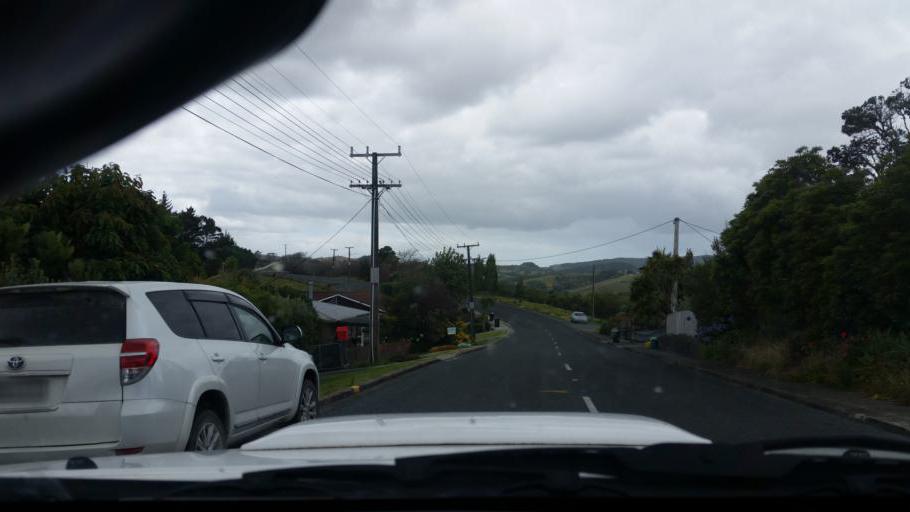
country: NZ
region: Northland
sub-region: Whangarei
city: Ruakaka
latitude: -36.1056
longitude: 174.3494
